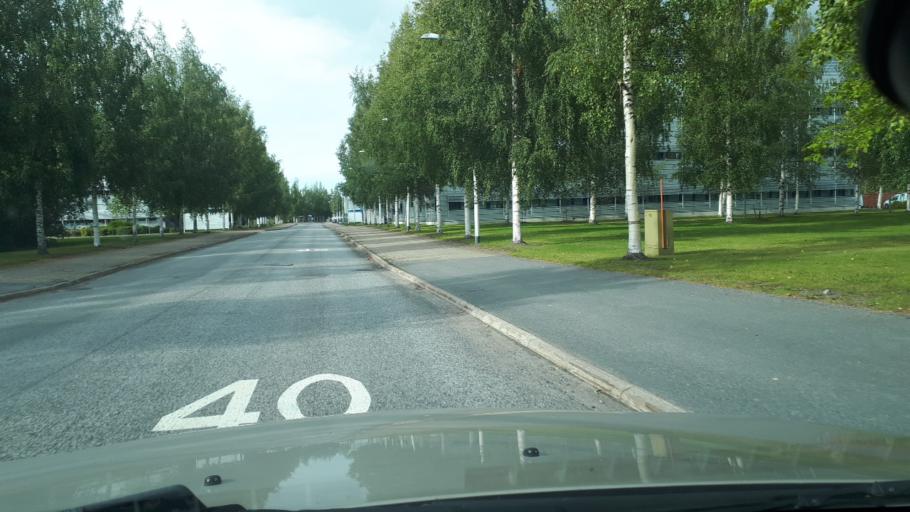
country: FI
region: Northern Ostrobothnia
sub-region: Oulu
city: Oulu
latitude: 65.0579
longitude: 25.4418
